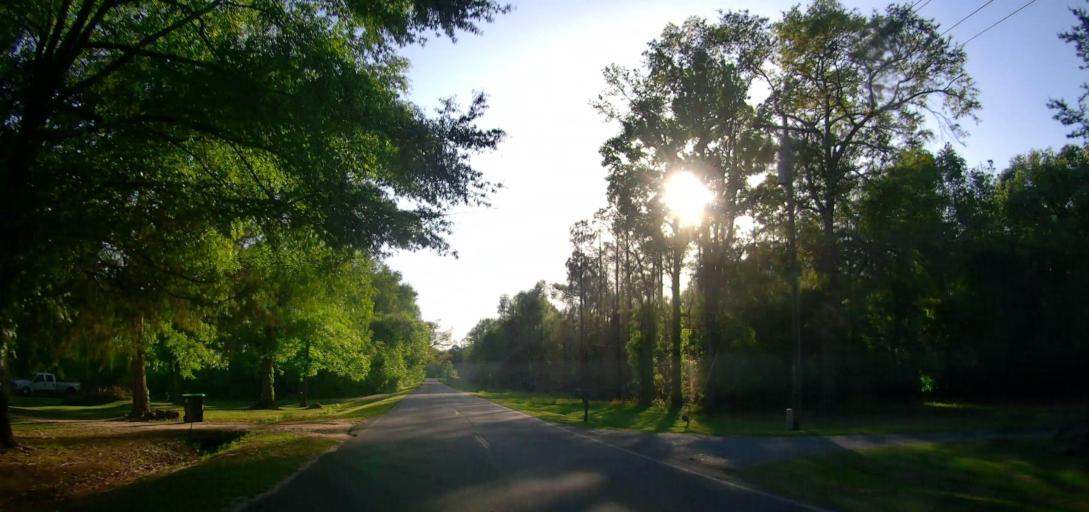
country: US
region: Georgia
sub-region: Macon County
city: Oglethorpe
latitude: 32.2888
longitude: -84.0819
